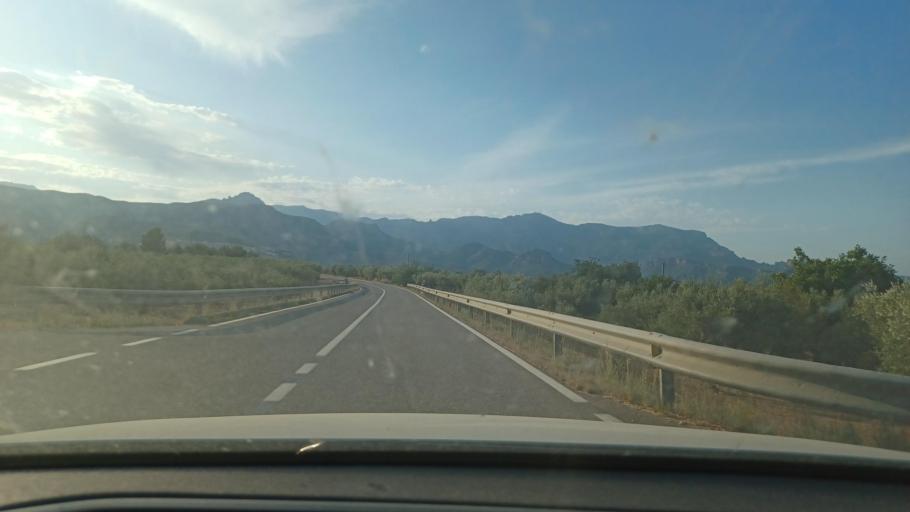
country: ES
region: Catalonia
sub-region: Provincia de Tarragona
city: Mas de Barberans
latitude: 40.7213
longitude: 0.3963
